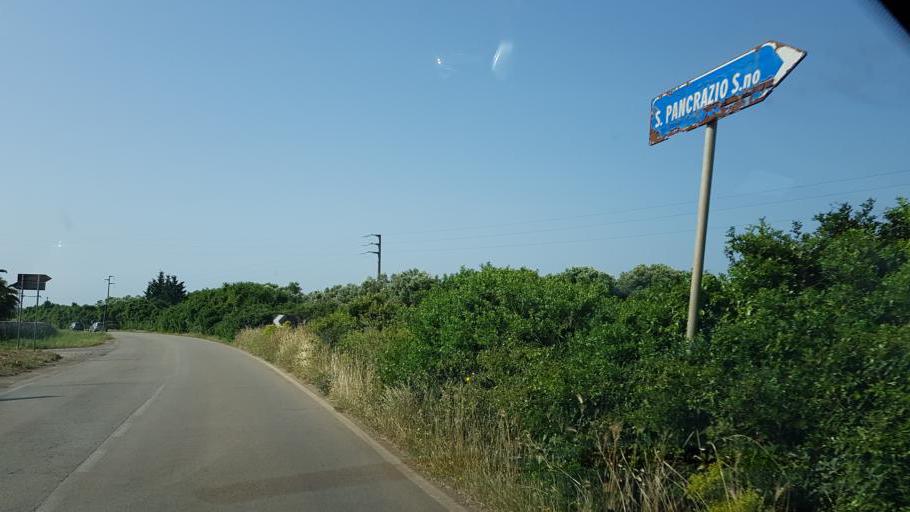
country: IT
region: Apulia
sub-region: Provincia di Lecce
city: Porto Cesareo
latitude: 40.3264
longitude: 17.8534
